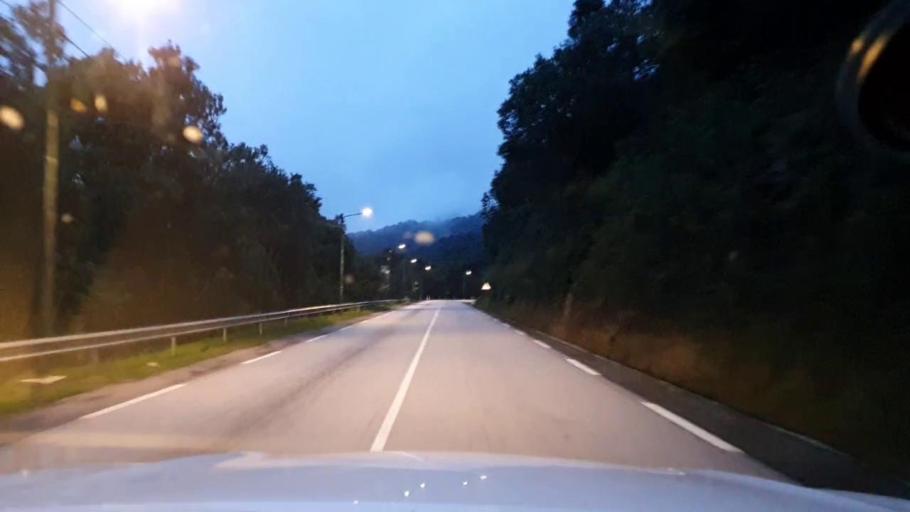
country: RW
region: Southern Province
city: Nzega
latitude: -2.5276
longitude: 29.3799
